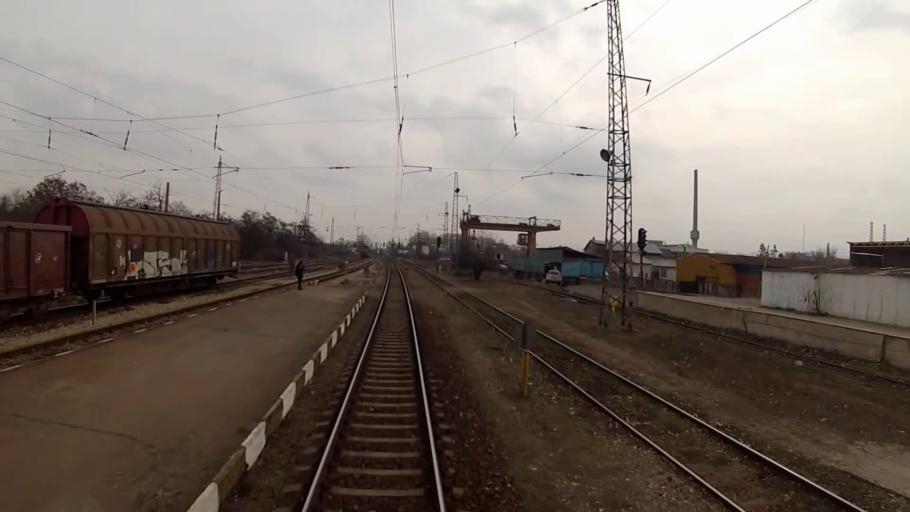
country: BG
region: Sofia-Capital
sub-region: Stolichna Obshtina
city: Sofia
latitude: 42.6576
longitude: 23.4457
